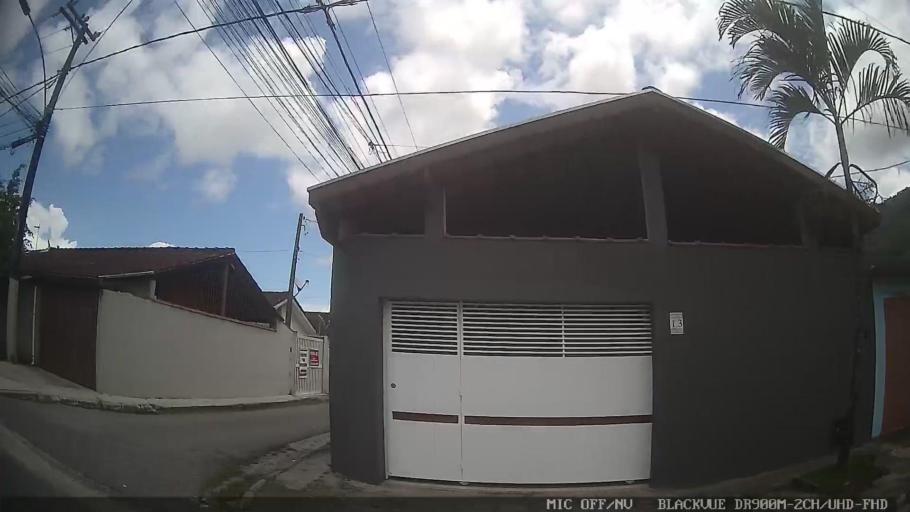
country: BR
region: Sao Paulo
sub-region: Caraguatatuba
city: Caraguatatuba
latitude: -23.6123
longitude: -45.3796
